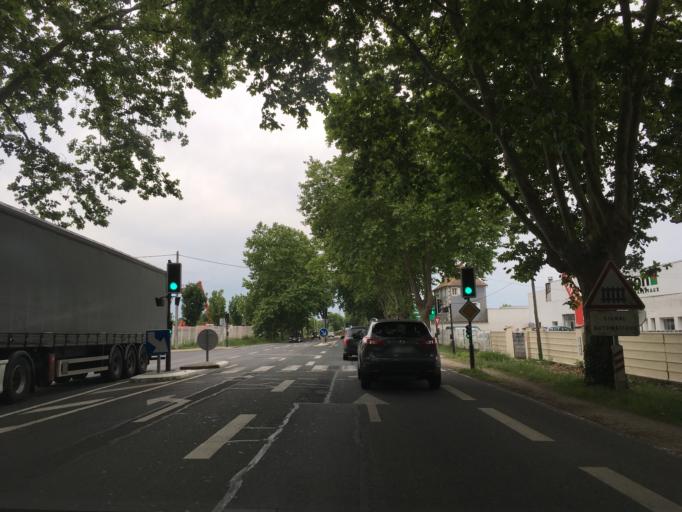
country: FR
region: Poitou-Charentes
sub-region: Departement des Deux-Sevres
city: Bessines
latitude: 46.3073
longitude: -0.4855
